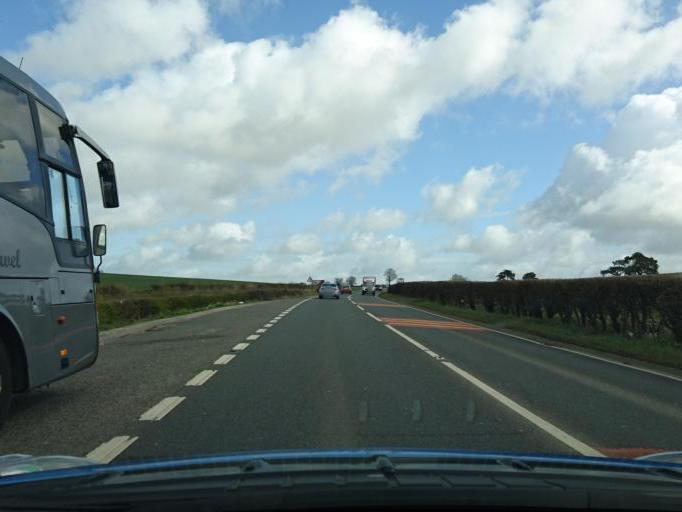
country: GB
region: England
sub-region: South Gloucestershire
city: Cold Ashton
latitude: 51.4629
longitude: -2.3669
